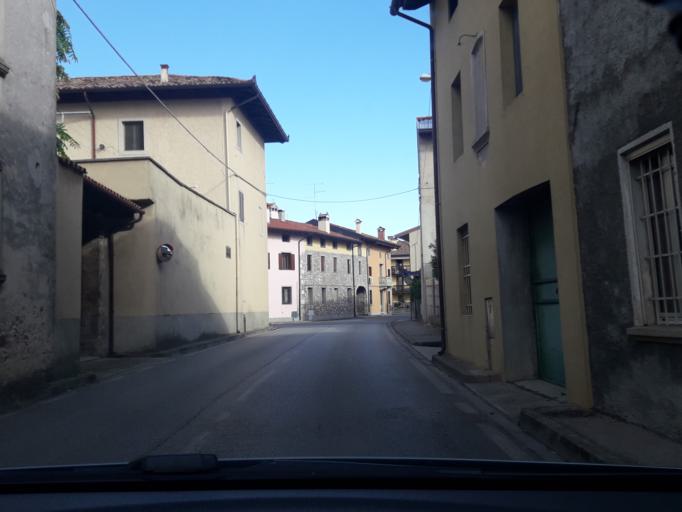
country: IT
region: Friuli Venezia Giulia
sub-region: Provincia di Udine
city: Passons
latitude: 46.0687
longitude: 13.1871
